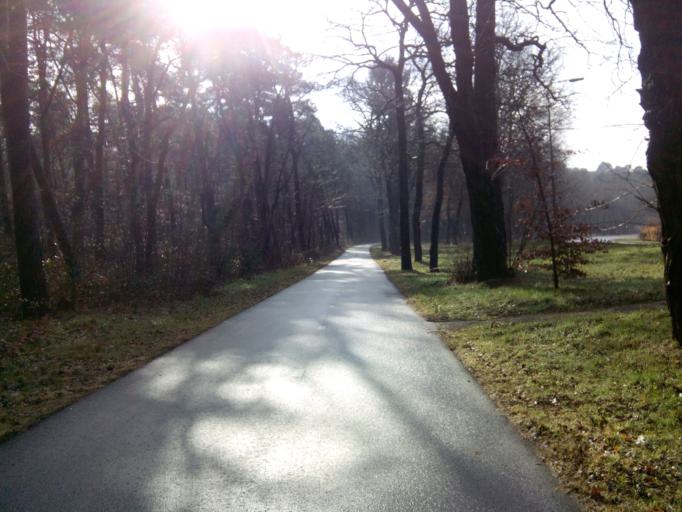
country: NL
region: Utrecht
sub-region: Gemeente Utrechtse Heuvelrug
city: Leersum
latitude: 52.0214
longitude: 5.4195
